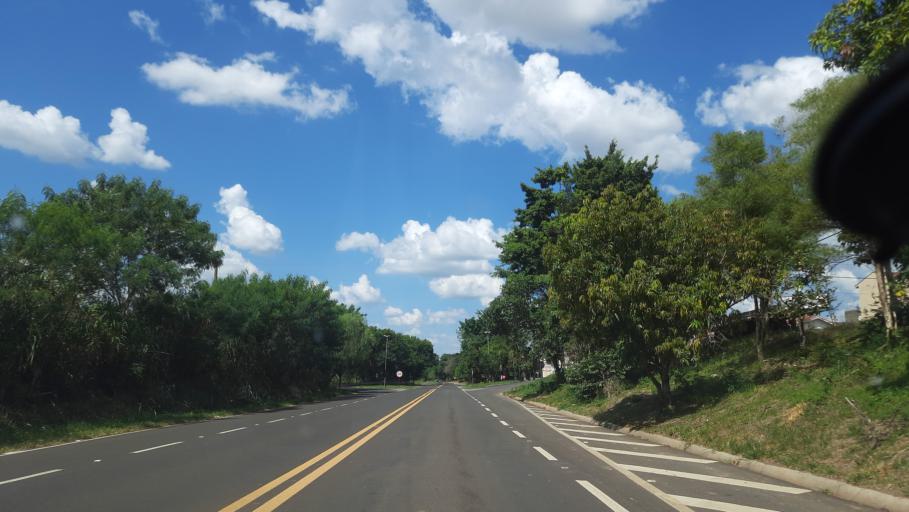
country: BR
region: Sao Paulo
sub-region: Sao Jose Do Rio Pardo
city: Sao Jose do Rio Pardo
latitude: -21.6065
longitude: -46.9332
